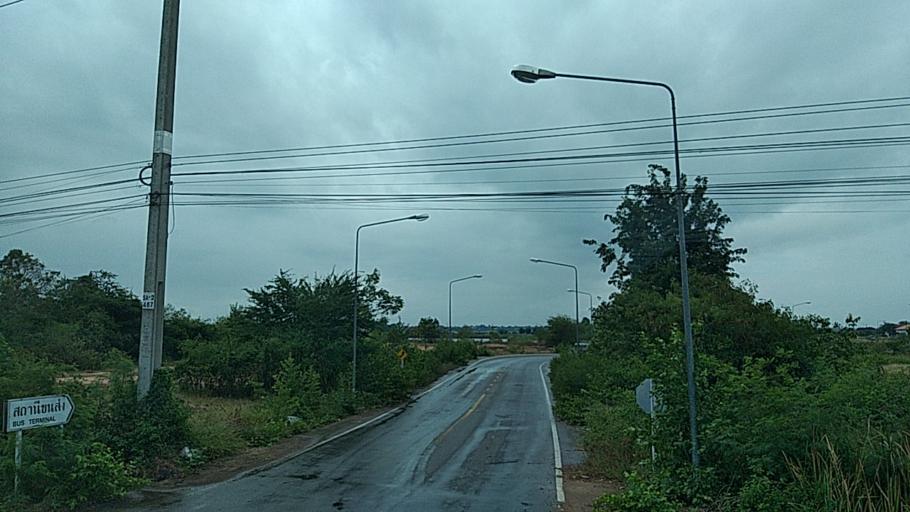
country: TH
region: Maha Sarakham
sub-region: Amphoe Borabue
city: Borabue
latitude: 16.0412
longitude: 103.1287
